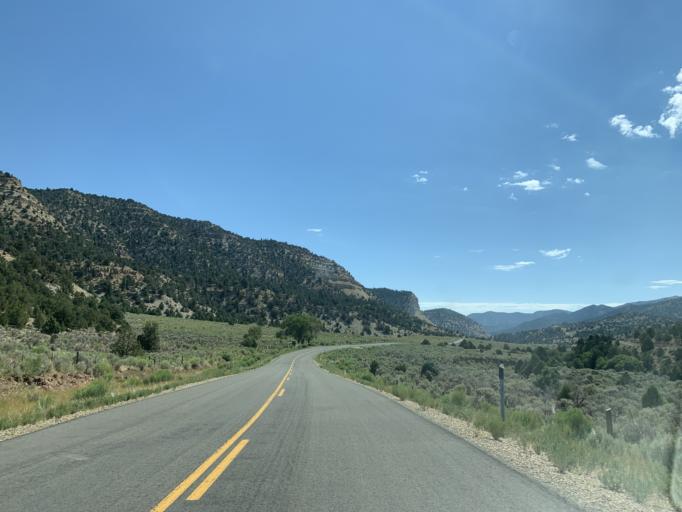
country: US
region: Utah
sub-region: Carbon County
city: East Carbon City
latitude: 39.7760
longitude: -110.5021
